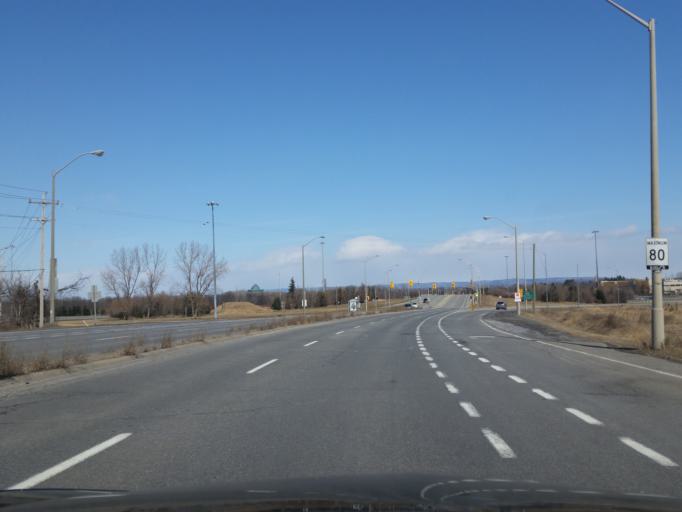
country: CA
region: Ontario
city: Bells Corners
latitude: 45.3348
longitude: -75.8404
